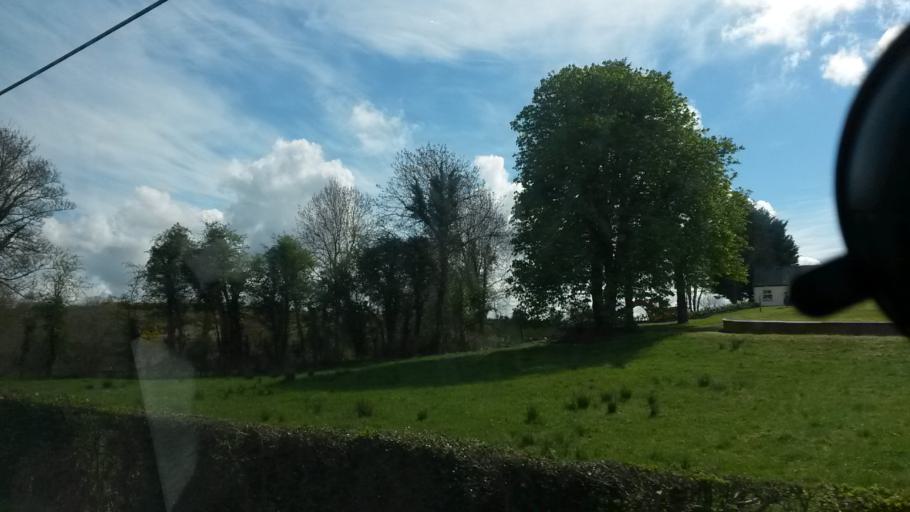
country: IE
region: Ulster
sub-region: An Cabhan
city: Ballyconnell
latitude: 54.1576
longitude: -7.5214
